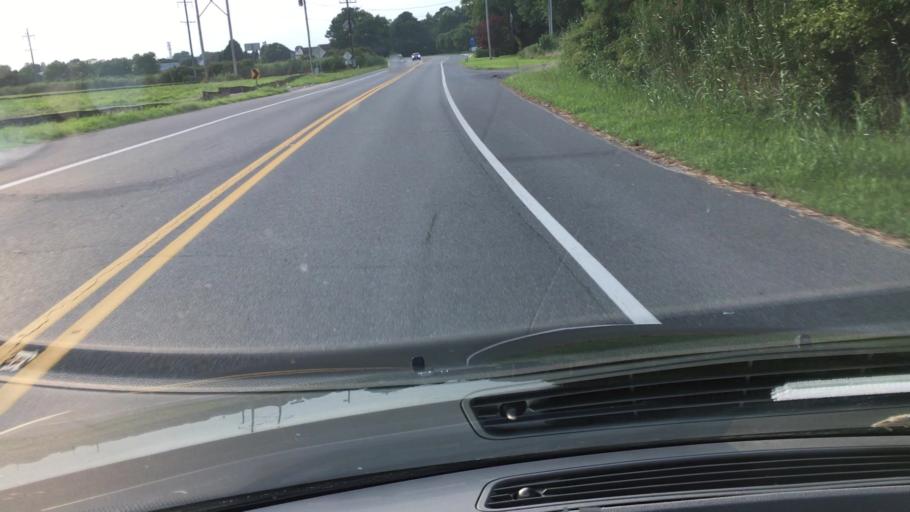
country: US
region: Delaware
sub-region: Sussex County
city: Bethany Beach
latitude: 38.5233
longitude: -75.0712
